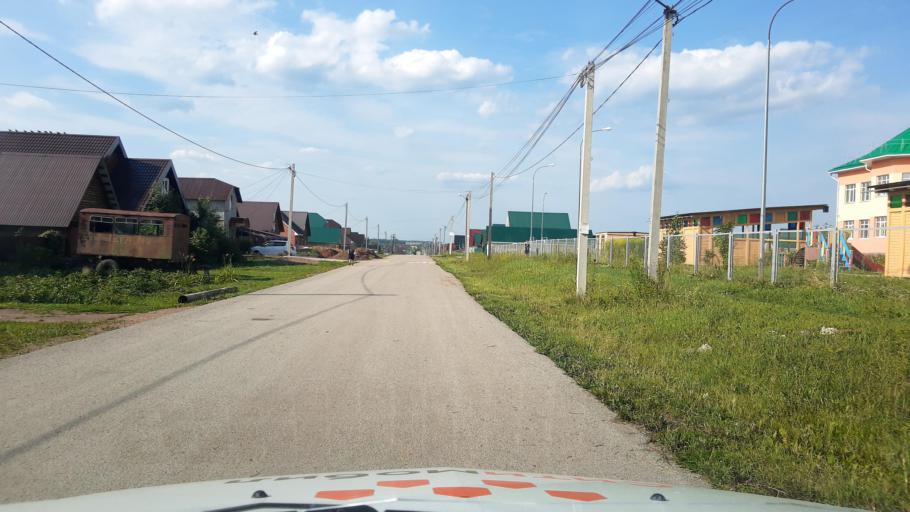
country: RU
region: Bashkortostan
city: Kabakovo
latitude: 54.6527
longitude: 56.2126
